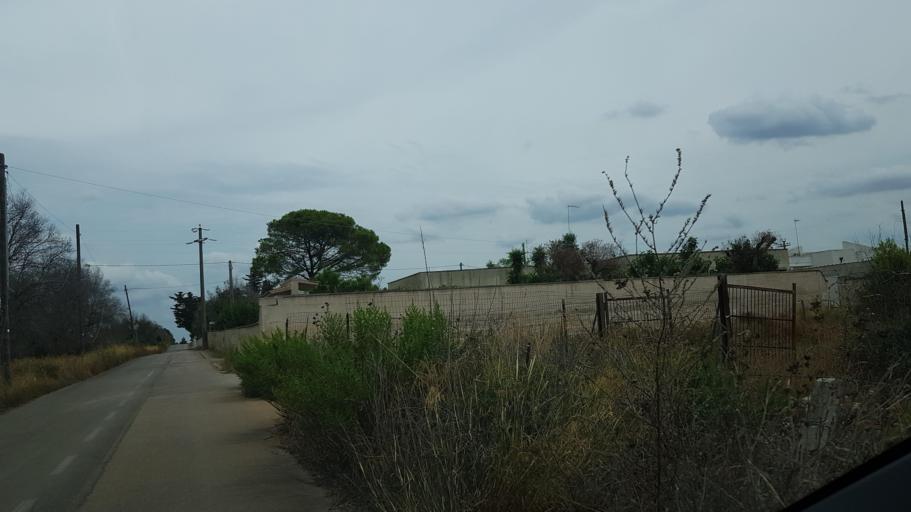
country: IT
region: Apulia
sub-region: Provincia di Lecce
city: Porto Cesareo
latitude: 40.2430
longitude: 17.9251
